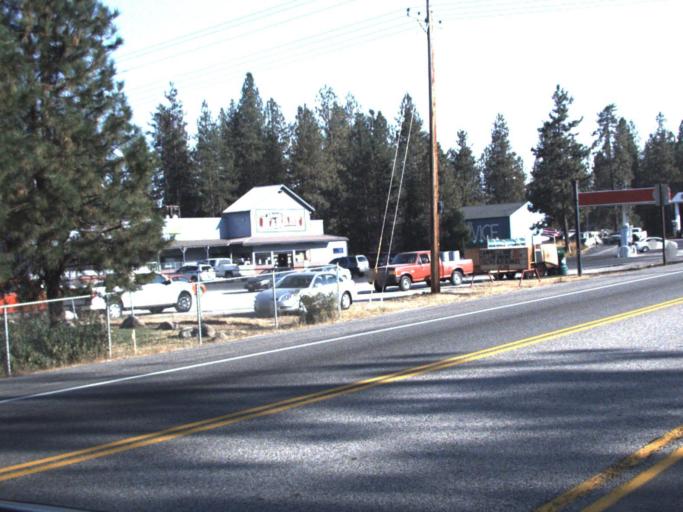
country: US
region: Washington
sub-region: Spokane County
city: Deer Park
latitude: 47.9715
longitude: -117.3496
